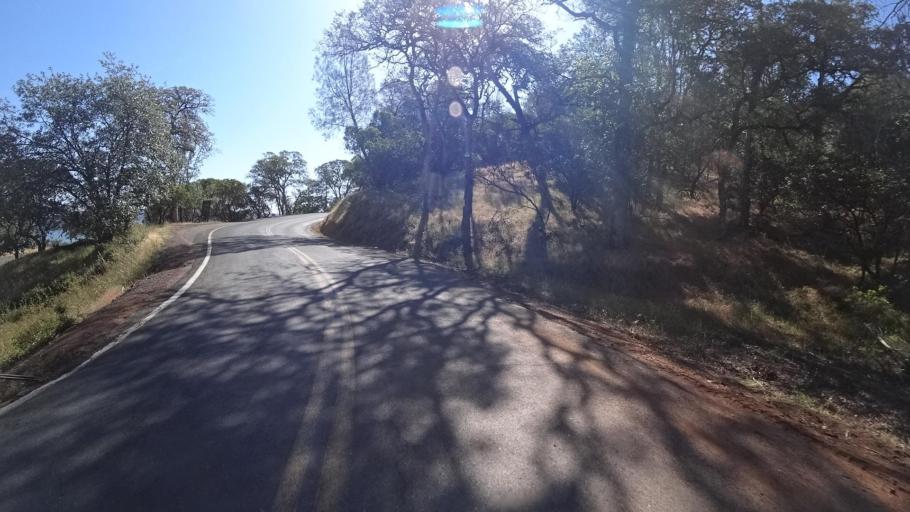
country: US
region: California
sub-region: Lake County
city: Clearlake Oaks
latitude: 39.0030
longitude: -122.7090
